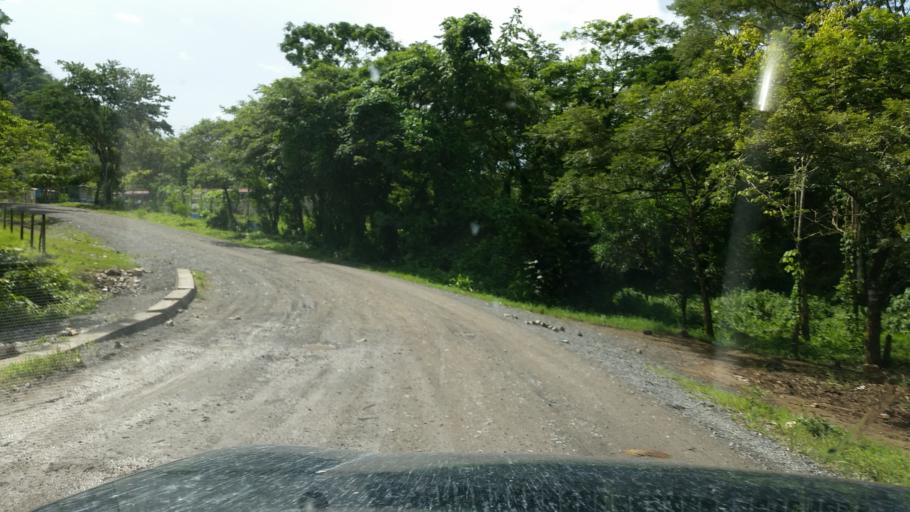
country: NI
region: Atlantico Norte (RAAN)
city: Siuna
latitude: 13.7179
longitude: -84.7636
